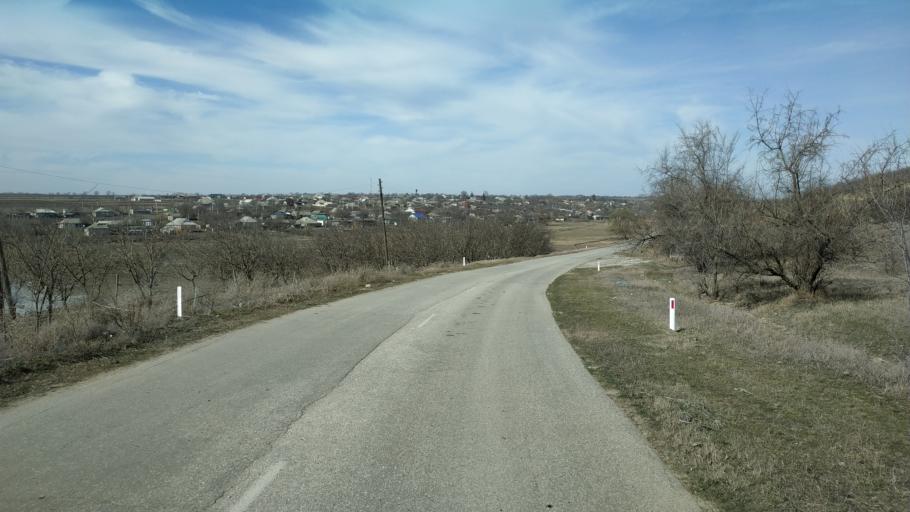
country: MD
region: Nisporeni
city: Nisporeni
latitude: 46.9556
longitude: 28.2225
